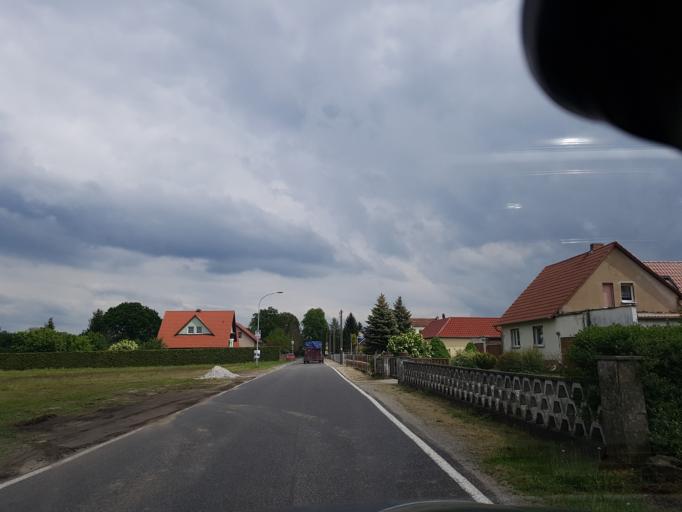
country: DE
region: Brandenburg
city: Finsterwalde
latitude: 51.6583
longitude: 13.7762
